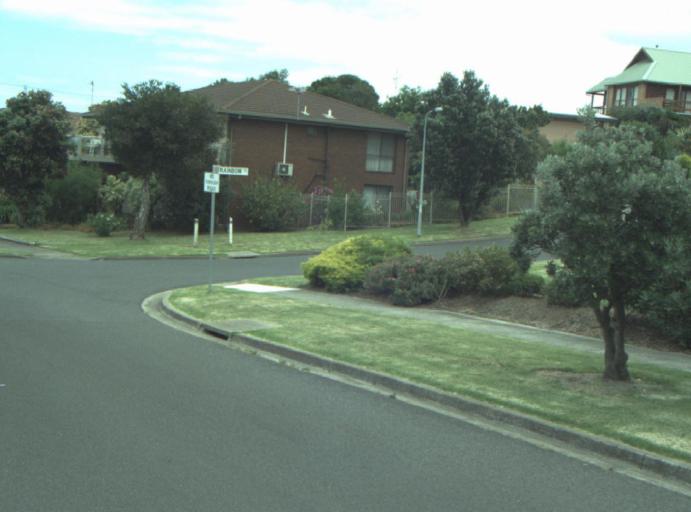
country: AU
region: Victoria
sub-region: Greater Geelong
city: Leopold
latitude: -38.2656
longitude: 144.5371
